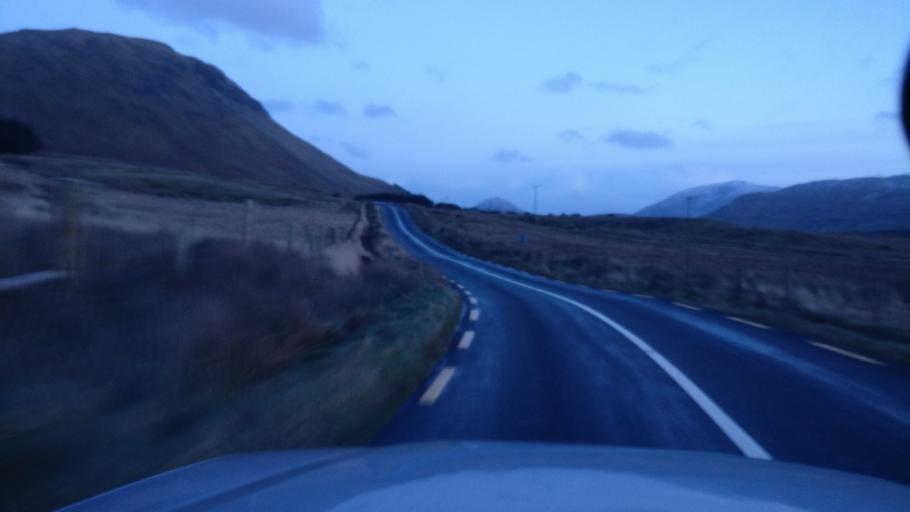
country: IE
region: Connaught
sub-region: Maigh Eo
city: Westport
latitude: 53.5506
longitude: -9.6337
